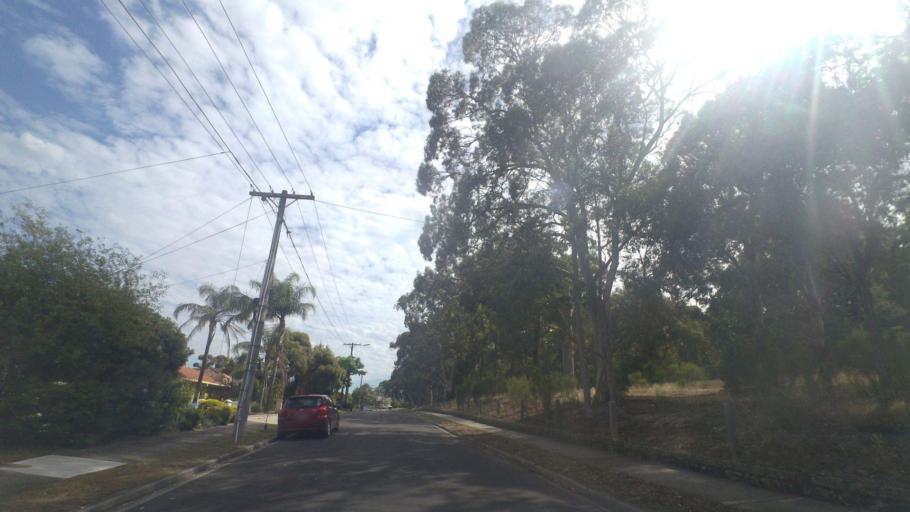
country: AU
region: Victoria
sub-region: Banyule
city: Viewbank
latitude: -37.7361
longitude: 145.0853
